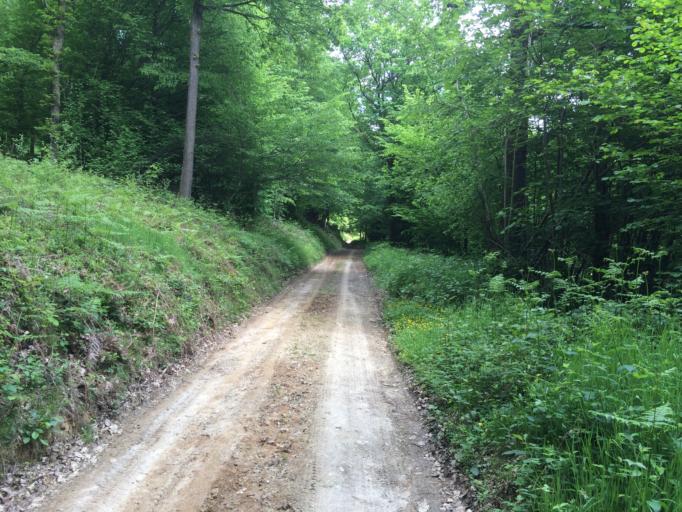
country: BE
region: Wallonia
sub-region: Province de Namur
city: Yvoir
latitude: 50.3321
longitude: 4.9502
